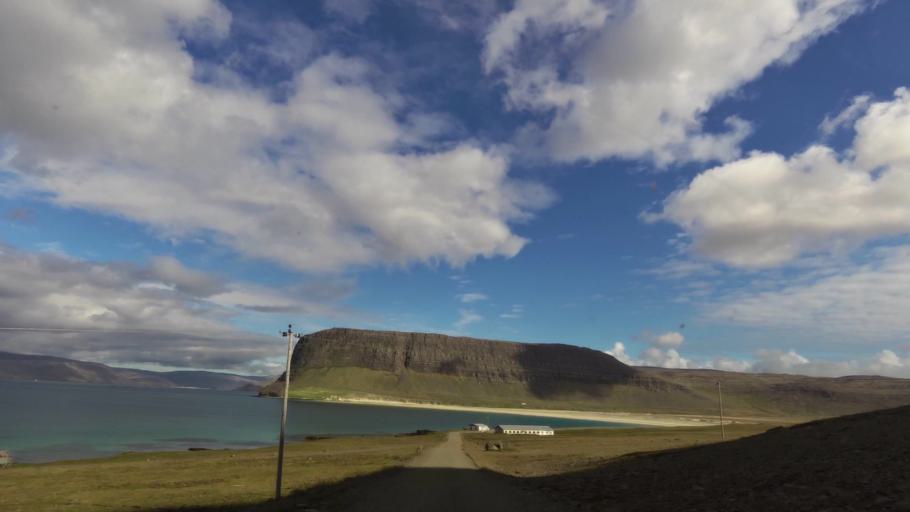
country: IS
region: West
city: Olafsvik
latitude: 65.5934
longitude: -24.1279
